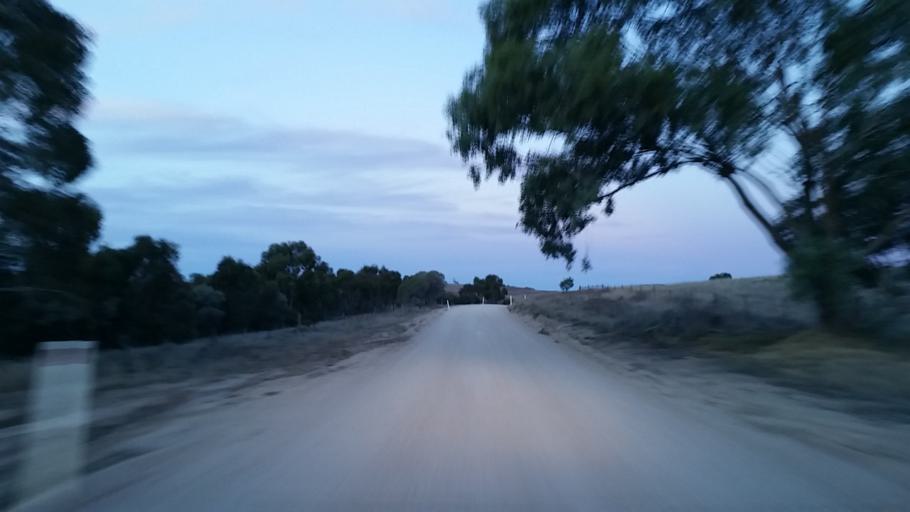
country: AU
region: South Australia
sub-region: Mount Barker
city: Callington
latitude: -35.0987
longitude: 138.9954
